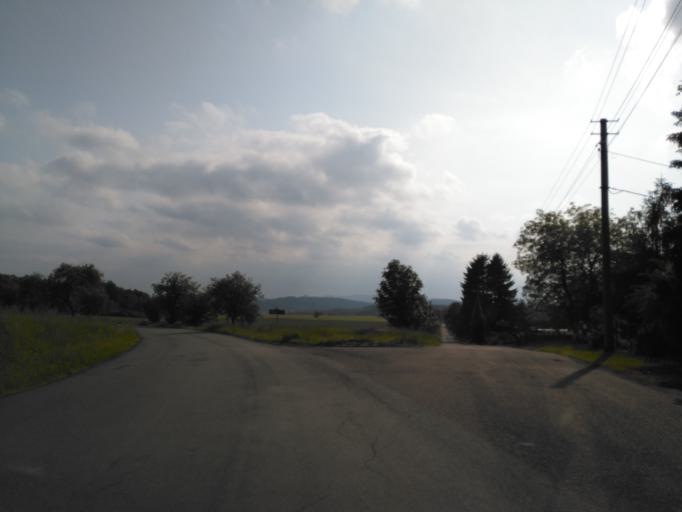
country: CZ
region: Plzensky
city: Zbiroh
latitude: 49.8826
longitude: 13.8010
